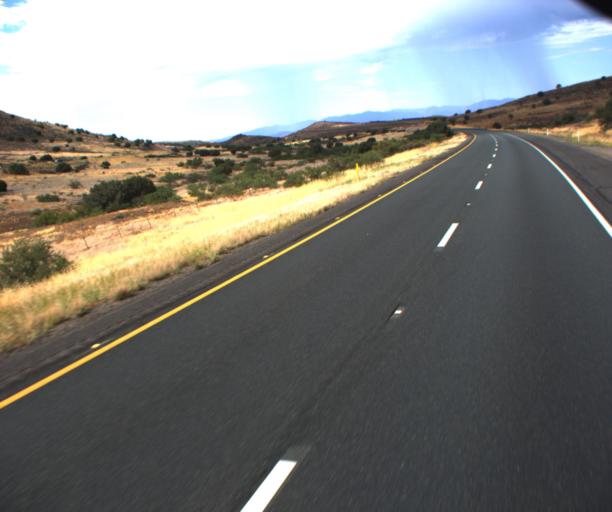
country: US
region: Arizona
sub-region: Yavapai County
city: Camp Verde
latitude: 34.4835
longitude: -112.0181
